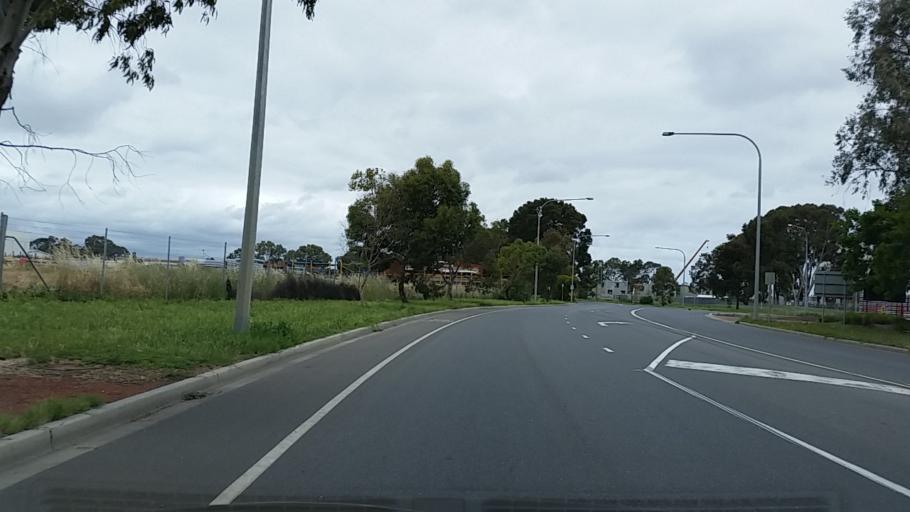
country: AU
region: South Australia
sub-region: Prospect
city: Prospect
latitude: -34.8710
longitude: 138.5757
